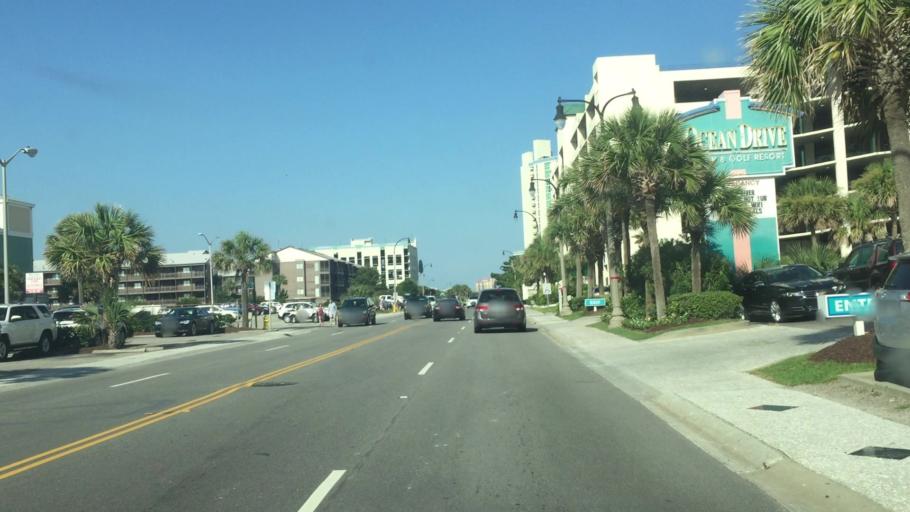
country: US
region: South Carolina
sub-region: Horry County
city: North Myrtle Beach
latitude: 33.8190
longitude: -78.6718
